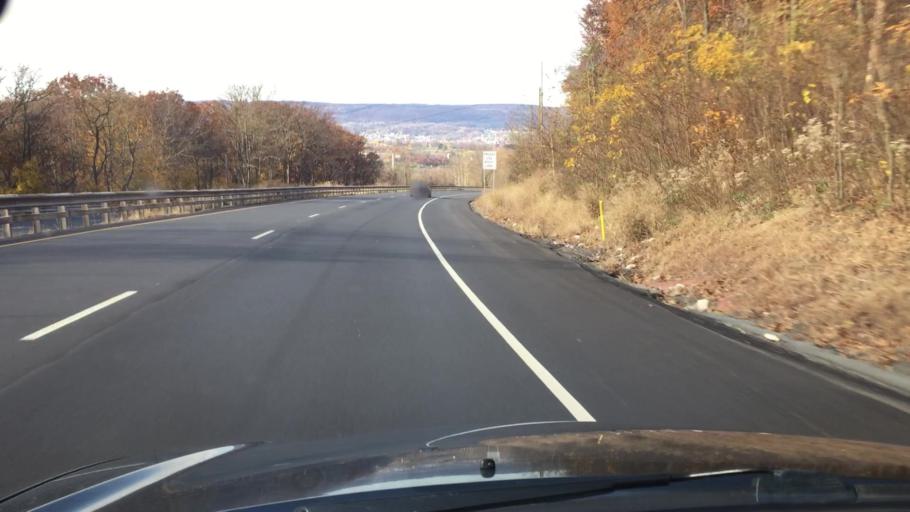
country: US
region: Pennsylvania
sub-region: Luzerne County
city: Ashley
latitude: 41.1988
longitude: -75.8933
